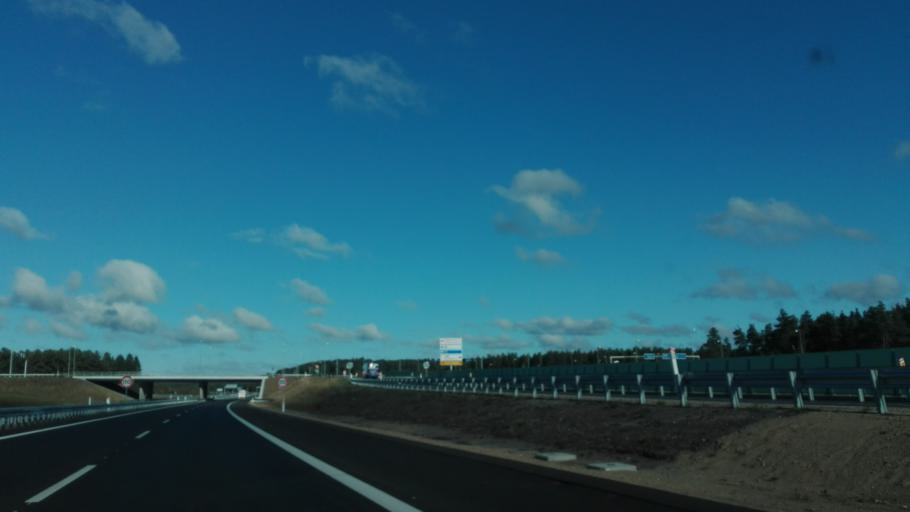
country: DK
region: Central Jutland
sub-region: Silkeborg Kommune
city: Svejbaek
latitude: 56.1672
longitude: 9.6040
